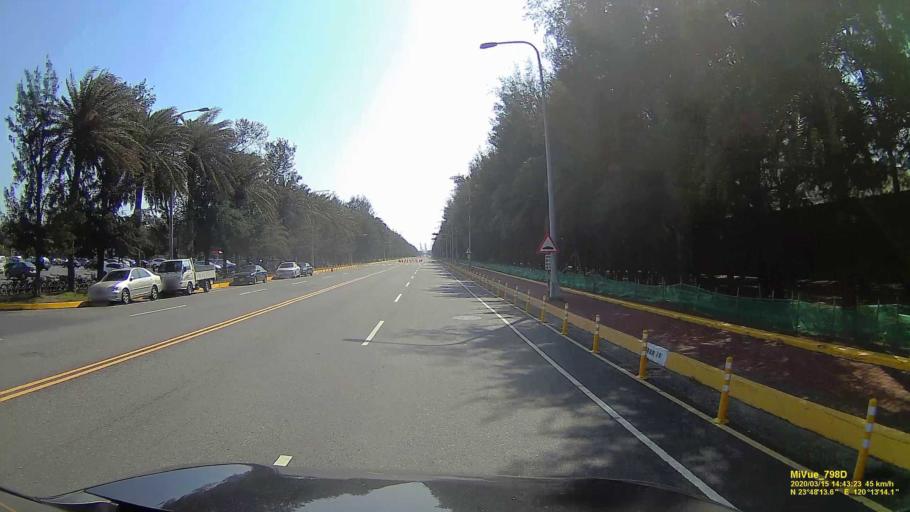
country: TW
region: Taiwan
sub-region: Yunlin
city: Douliu
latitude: 23.8037
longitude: 120.2205
